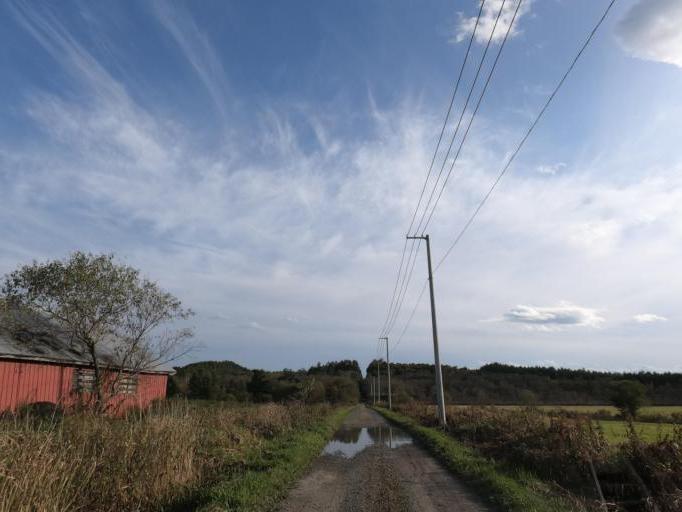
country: JP
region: Hokkaido
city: Obihiro
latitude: 42.5371
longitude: 143.3667
